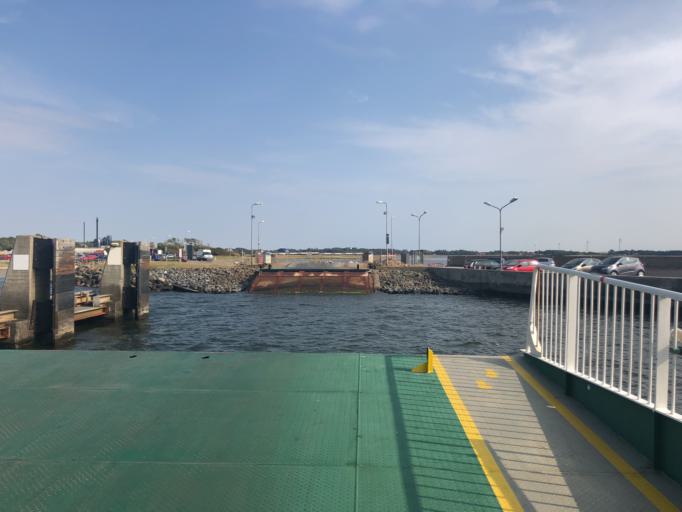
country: DK
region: North Denmark
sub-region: Morso Kommune
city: Nykobing Mors
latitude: 56.8007
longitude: 9.0253
